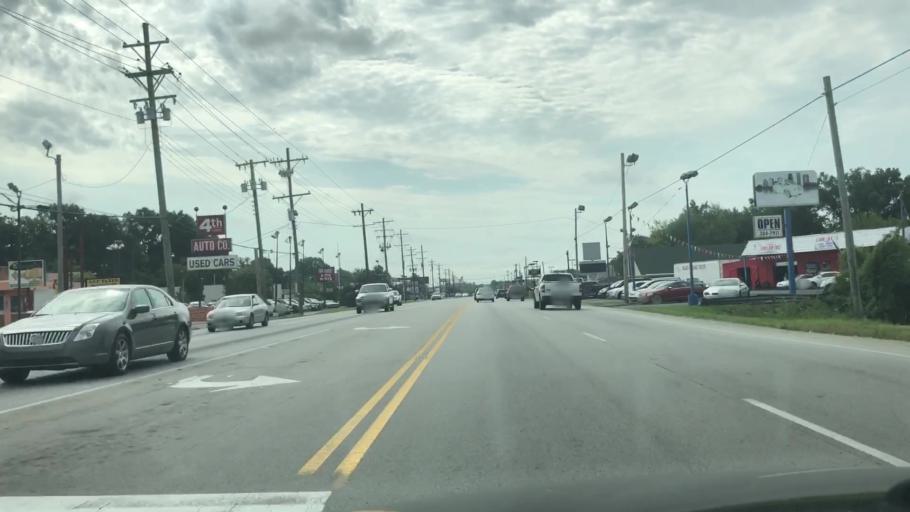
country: US
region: Kentucky
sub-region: Jefferson County
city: Audubon Park
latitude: 38.1745
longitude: -85.7127
